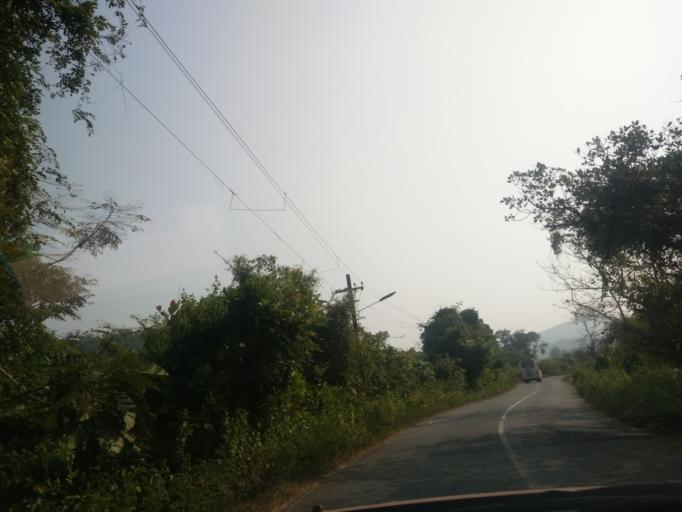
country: IN
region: Goa
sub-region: North Goa
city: Palle
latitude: 15.4641
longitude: 74.0725
